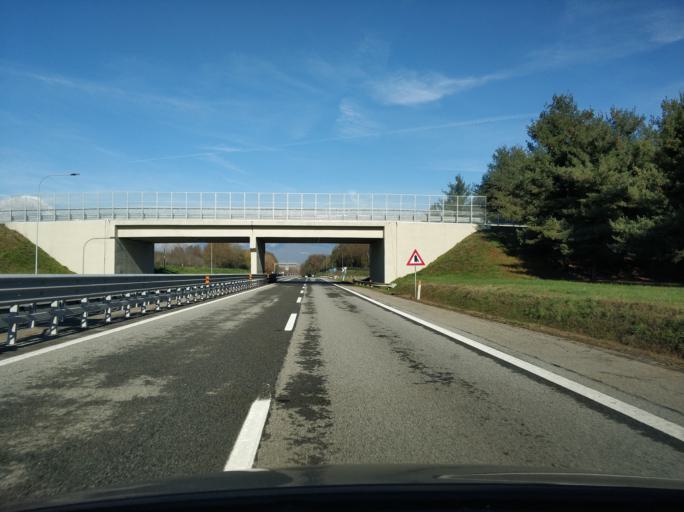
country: IT
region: Piedmont
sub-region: Provincia di Torino
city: Scarmagno
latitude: 45.3881
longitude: 7.8474
